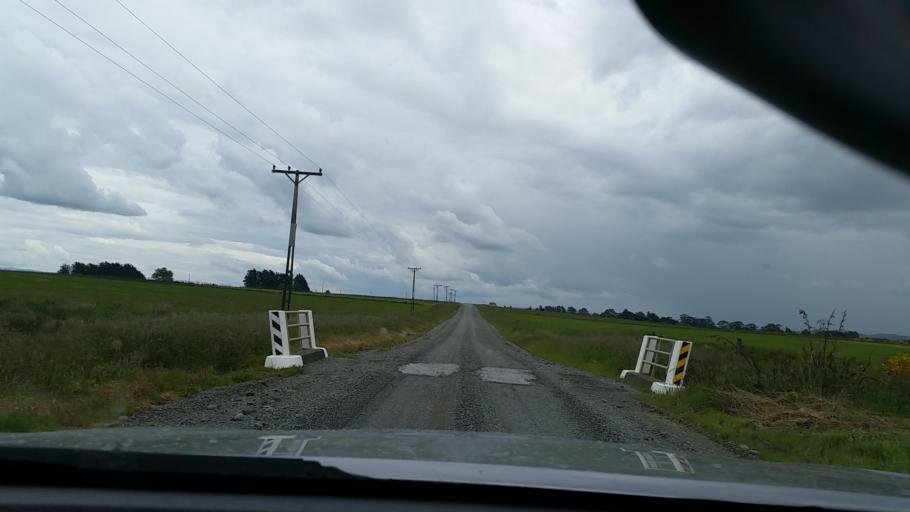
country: NZ
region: Southland
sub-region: Southland District
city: Winton
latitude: -46.0069
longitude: 168.2033
